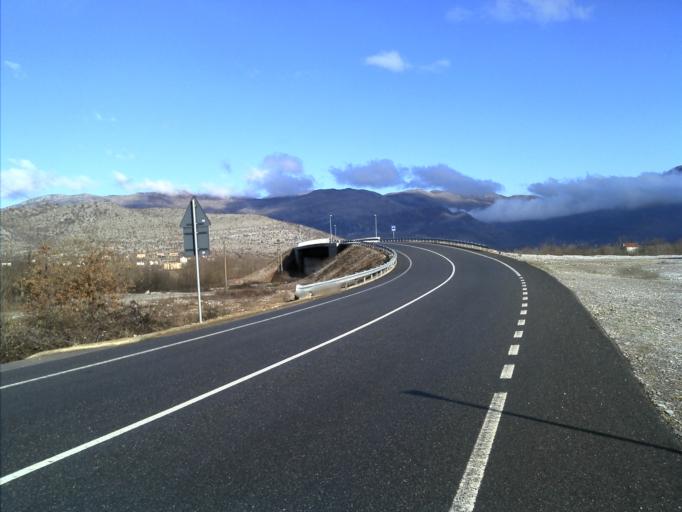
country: AL
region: Shkoder
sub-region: Rrethi i Malesia e Madhe
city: Hot
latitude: 42.3098
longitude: 19.4410
